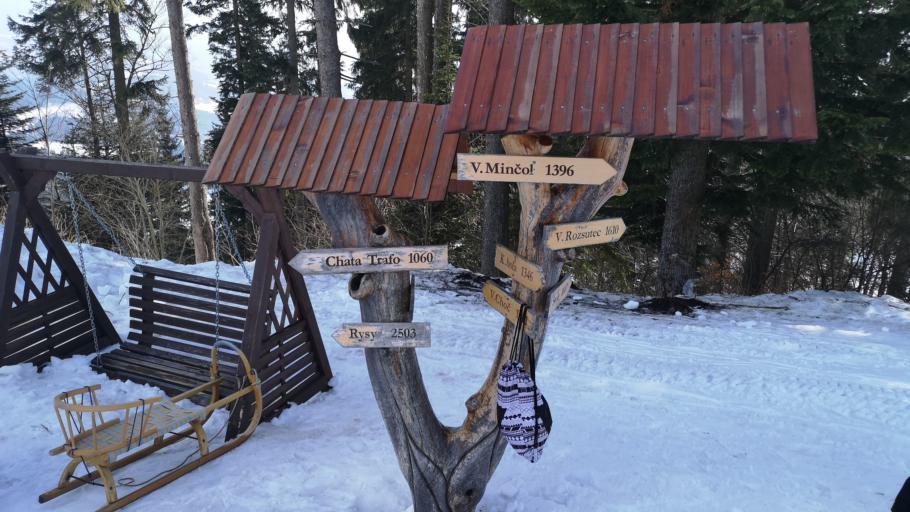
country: SK
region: Zilinsky
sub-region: Okres Dolny Kubin
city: Dolny Kubin
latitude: 49.2607
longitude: 19.2602
